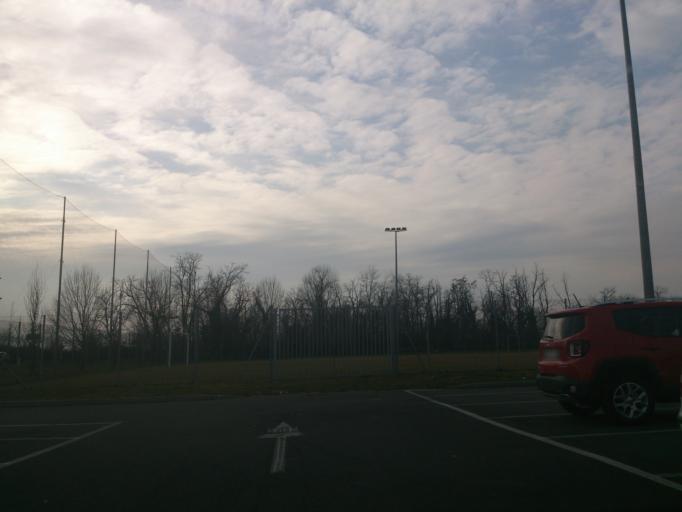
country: IT
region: Lombardy
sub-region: Citta metropolitana di Milano
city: Poasco-Sorigherio
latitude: 45.4068
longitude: 9.2288
